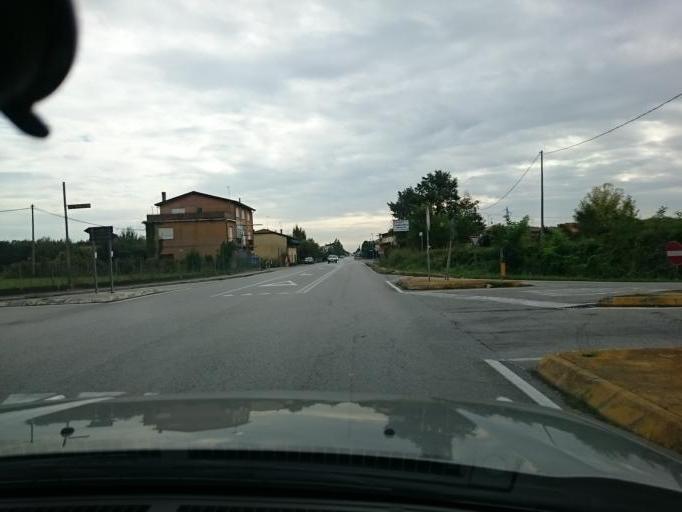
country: IT
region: Veneto
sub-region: Provincia di Padova
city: Legnaro
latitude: 45.3301
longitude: 11.9866
